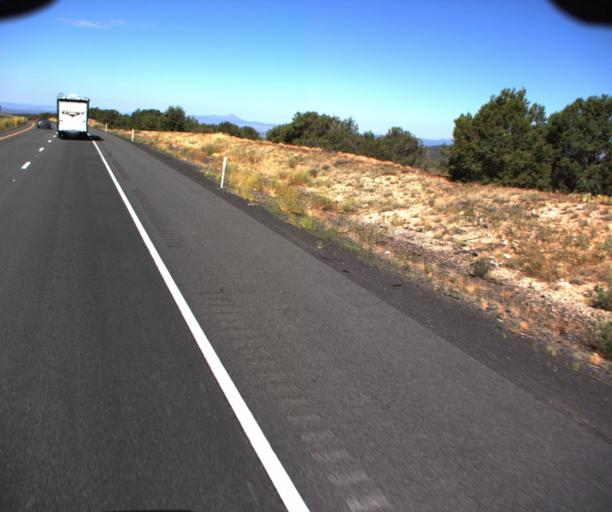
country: US
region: Arizona
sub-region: Coconino County
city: Williams
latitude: 35.2179
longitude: -112.3458
